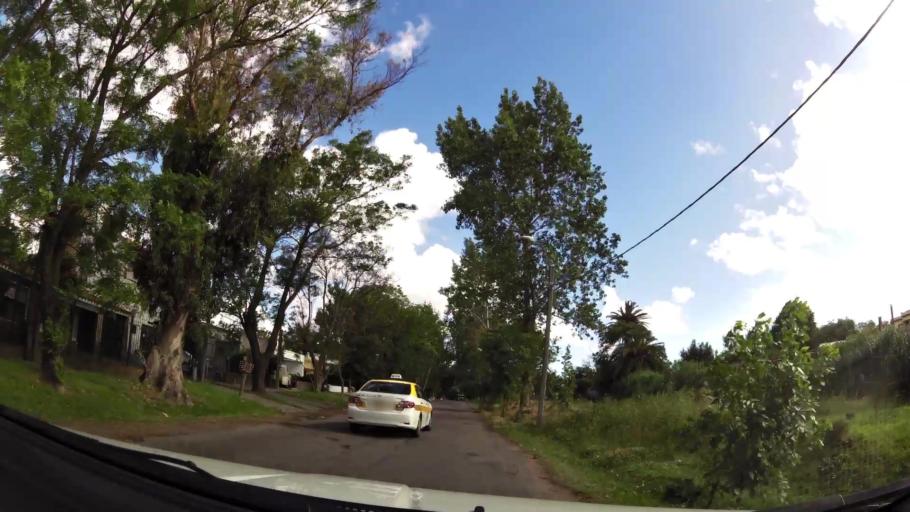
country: UY
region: Canelones
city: La Paz
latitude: -34.8104
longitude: -56.2201
